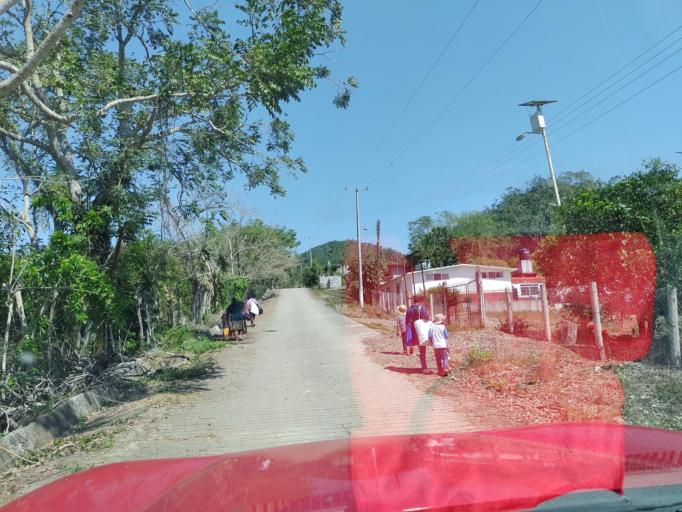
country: MX
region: Veracruz
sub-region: Papantla
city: Polutla
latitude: 20.5016
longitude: -97.2142
